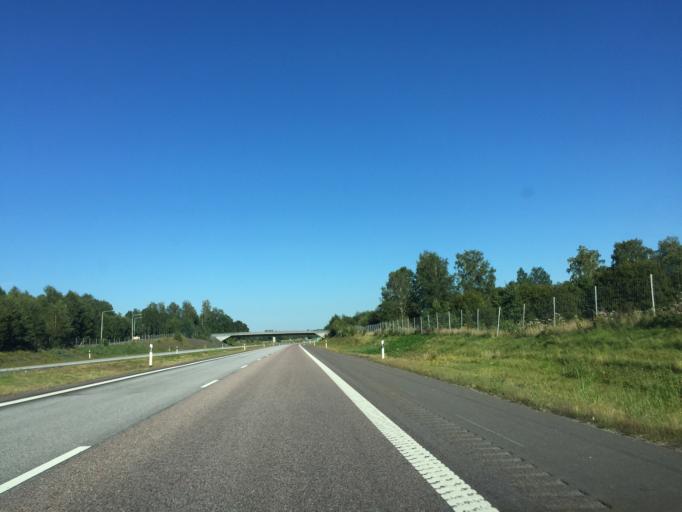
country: SE
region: OErebro
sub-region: Lindesbergs Kommun
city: Fellingsbro
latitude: 59.3273
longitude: 15.5029
